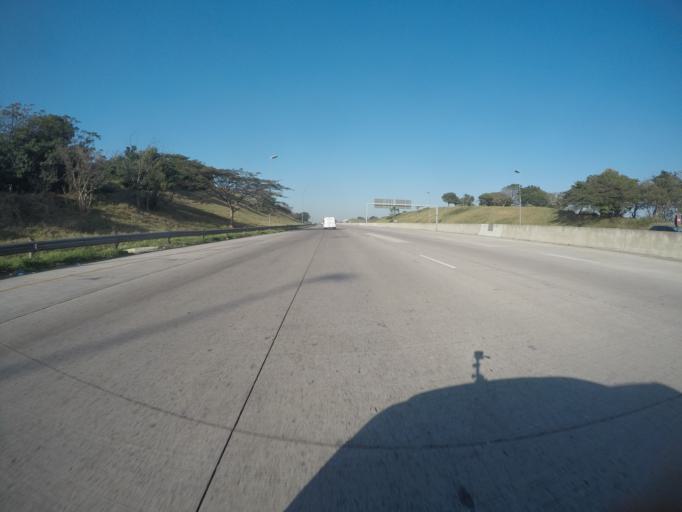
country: ZA
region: KwaZulu-Natal
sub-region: iLembe District Municipality
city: Ballitoville
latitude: -29.5902
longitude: 31.1405
